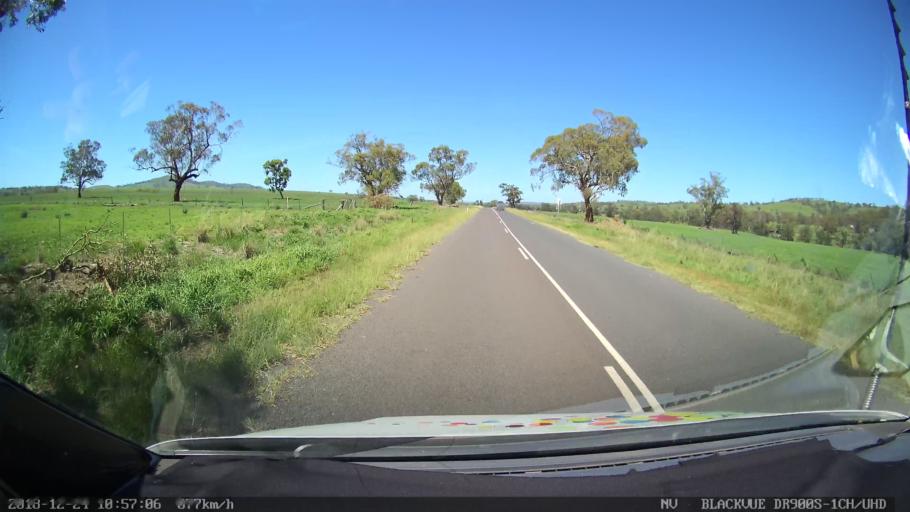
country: AU
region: New South Wales
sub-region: Upper Hunter Shire
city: Merriwa
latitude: -32.0327
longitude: 150.4156
